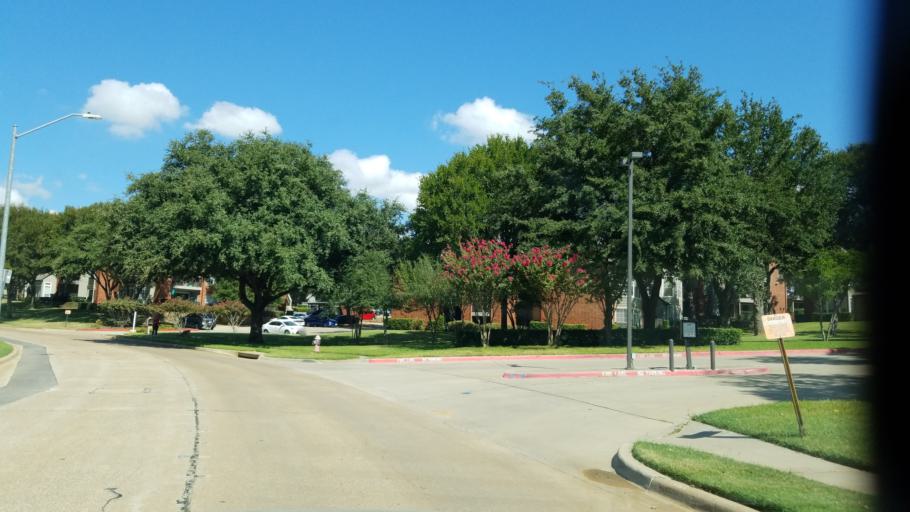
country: US
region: Texas
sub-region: Tarrant County
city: Euless
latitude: 32.8649
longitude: -97.0685
